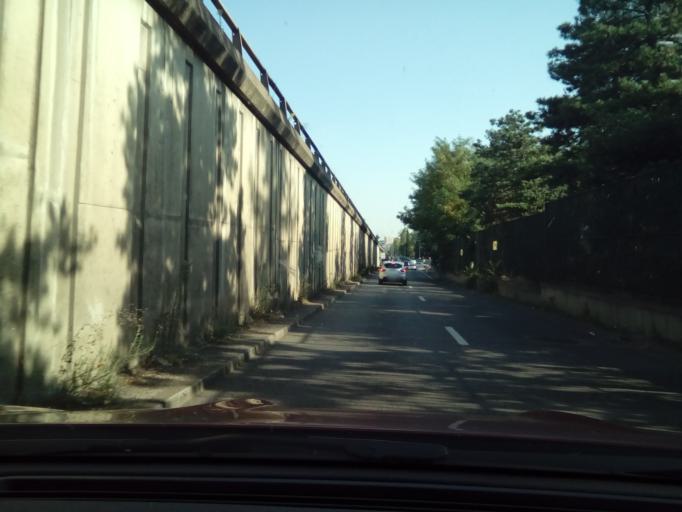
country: FR
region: Rhone-Alpes
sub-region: Departement du Rhone
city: Bron
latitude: 45.7491
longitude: 4.9074
